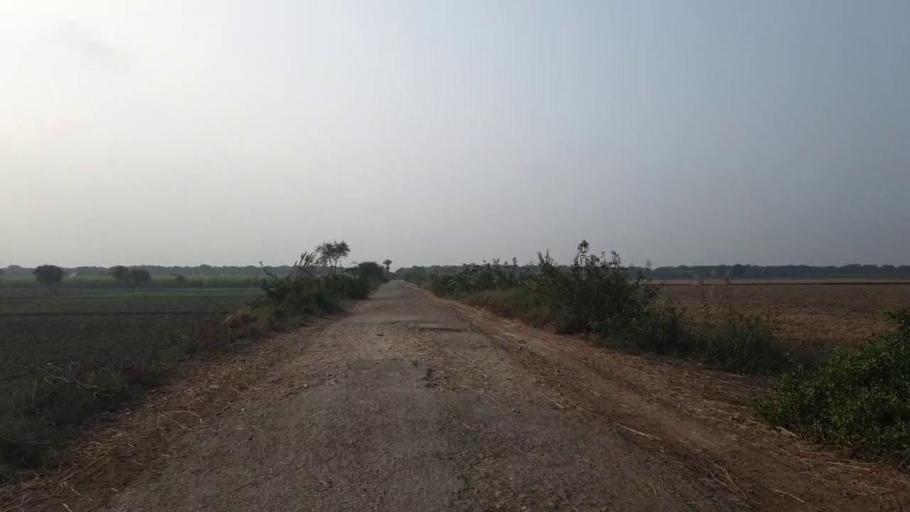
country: PK
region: Sindh
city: Tando Muhammad Khan
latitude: 25.1407
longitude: 68.6038
